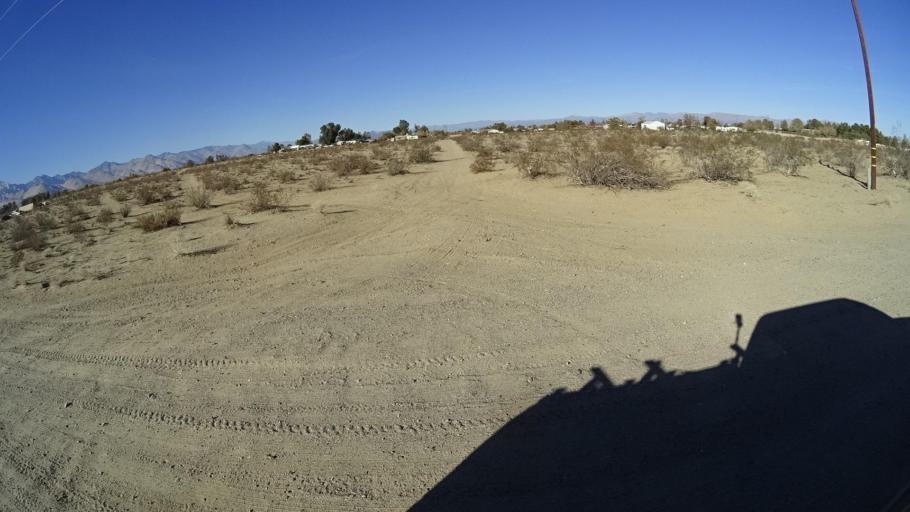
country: US
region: California
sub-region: Kern County
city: China Lake Acres
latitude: 35.6369
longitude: -117.7609
